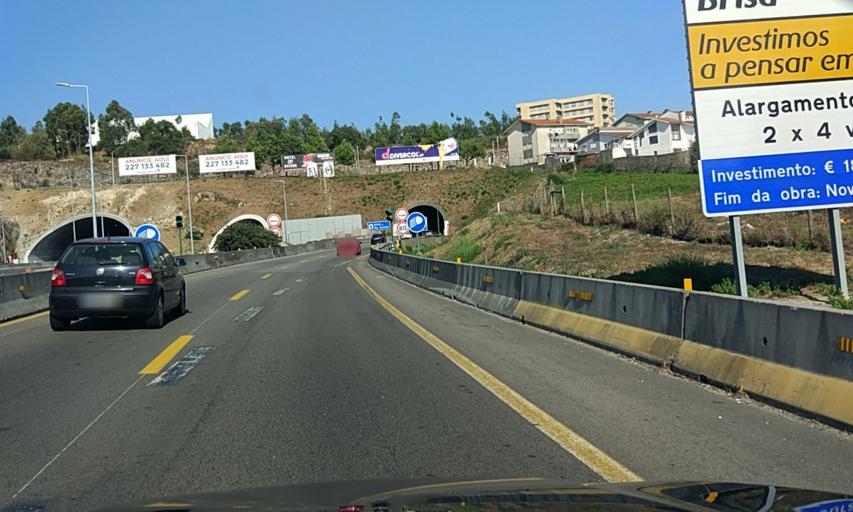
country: PT
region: Porto
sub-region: Maia
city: Pedroucos
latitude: 41.1981
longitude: -8.5799
